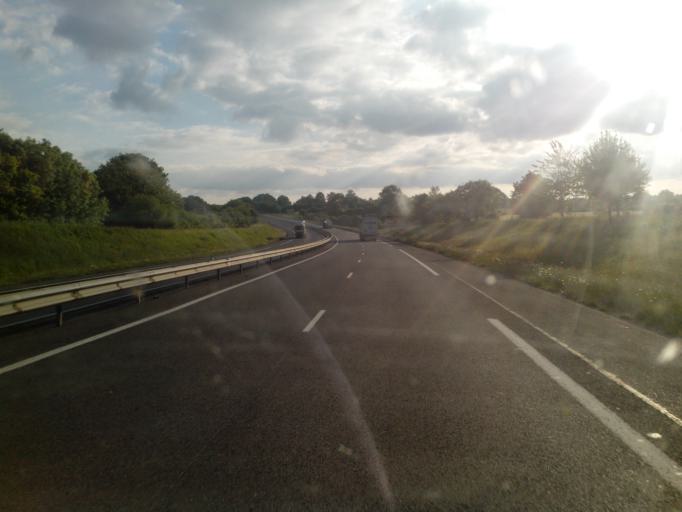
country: FR
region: Lower Normandy
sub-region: Departement du Calvados
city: Saint-Martin-des-Besaces
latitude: 49.0148
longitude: -0.8718
